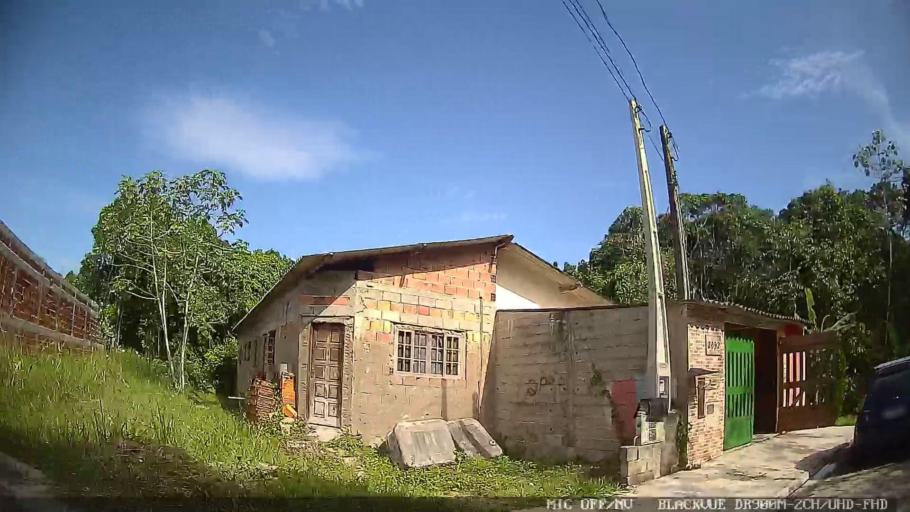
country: BR
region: Sao Paulo
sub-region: Itanhaem
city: Itanhaem
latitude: -24.1533
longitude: -46.7447
